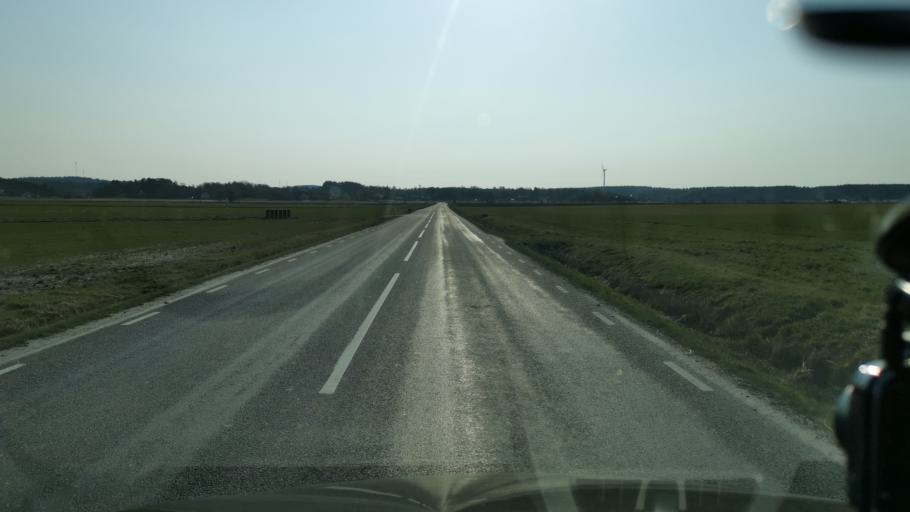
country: SE
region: Vaestra Goetaland
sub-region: Kungalvs Kommun
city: Kode
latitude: 57.9404
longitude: 11.8278
